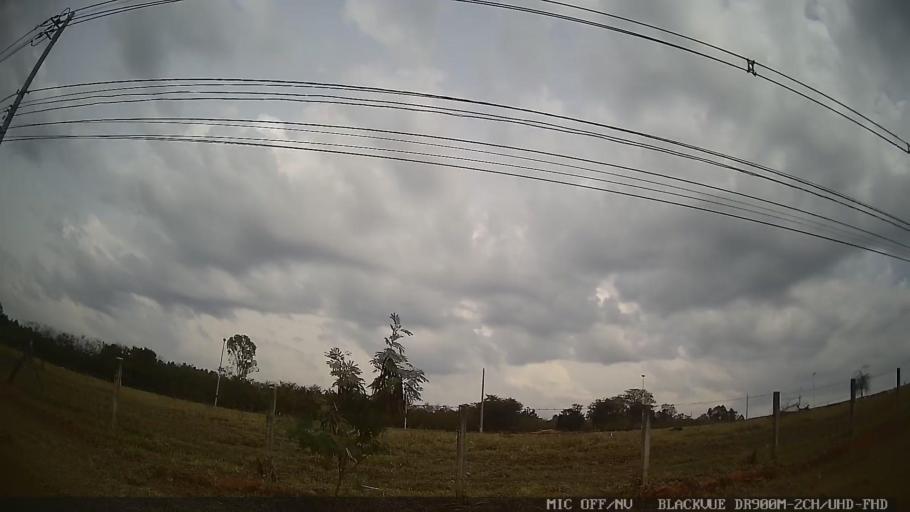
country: BR
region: Sao Paulo
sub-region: Indaiatuba
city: Indaiatuba
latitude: -23.1302
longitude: -47.2530
